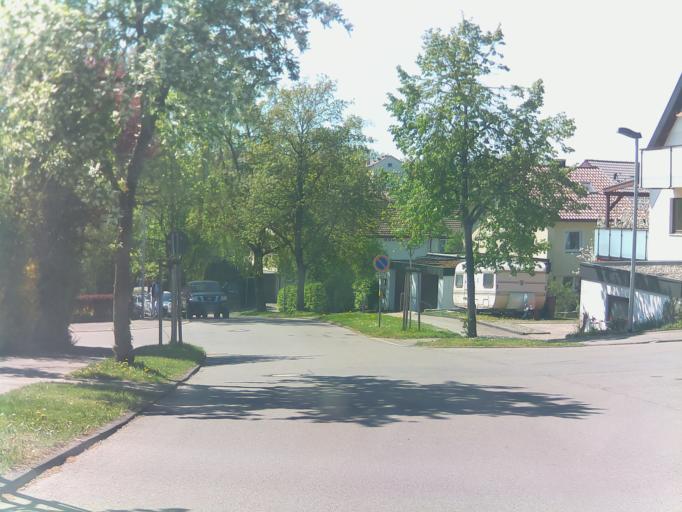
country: DE
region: Baden-Wuerttemberg
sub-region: Freiburg Region
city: Rottweil
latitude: 48.1598
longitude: 8.6213
